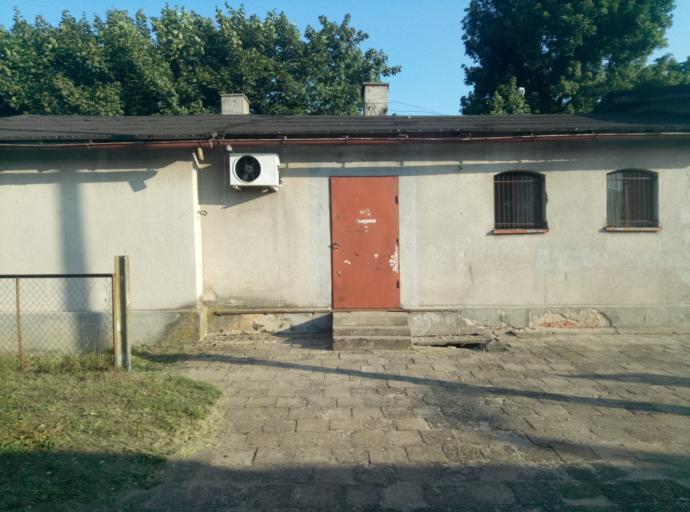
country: PL
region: Kujawsko-Pomorskie
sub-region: Powiat golubsko-dobrzynski
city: Kowalewo Pomorskie
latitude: 53.1418
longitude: 18.8140
